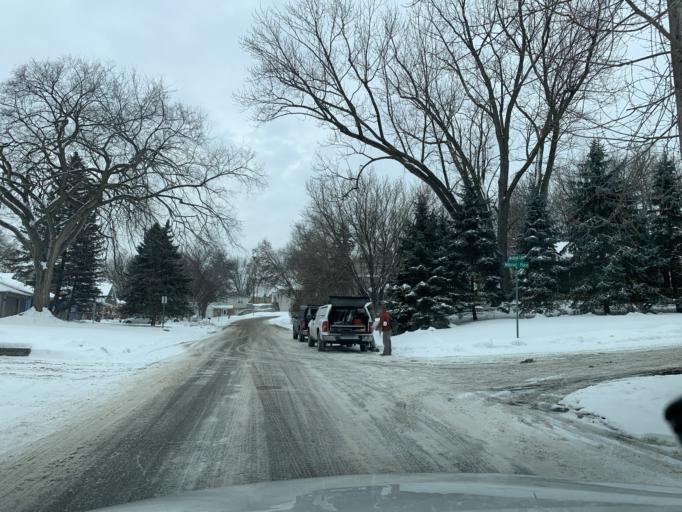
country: US
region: Minnesota
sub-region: Hennepin County
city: Edina
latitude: 44.9143
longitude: -93.3520
